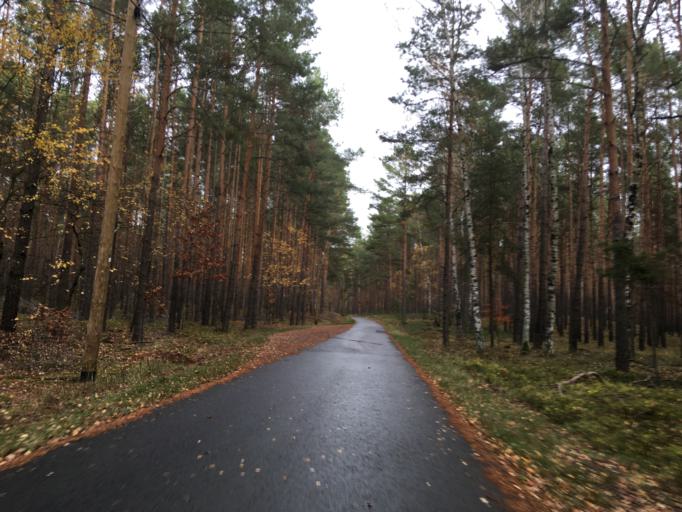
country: DE
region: Brandenburg
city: Tauer
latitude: 51.9156
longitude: 14.4671
